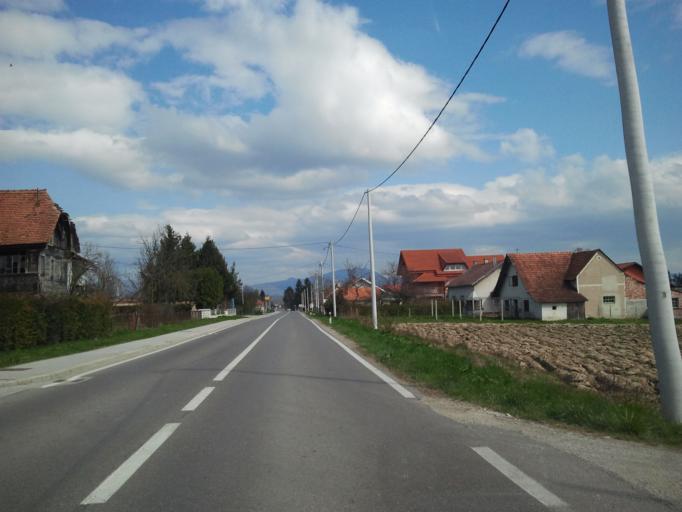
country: HR
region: Zagrebacka
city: Jastrebarsko
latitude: 45.5998
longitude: 15.5987
